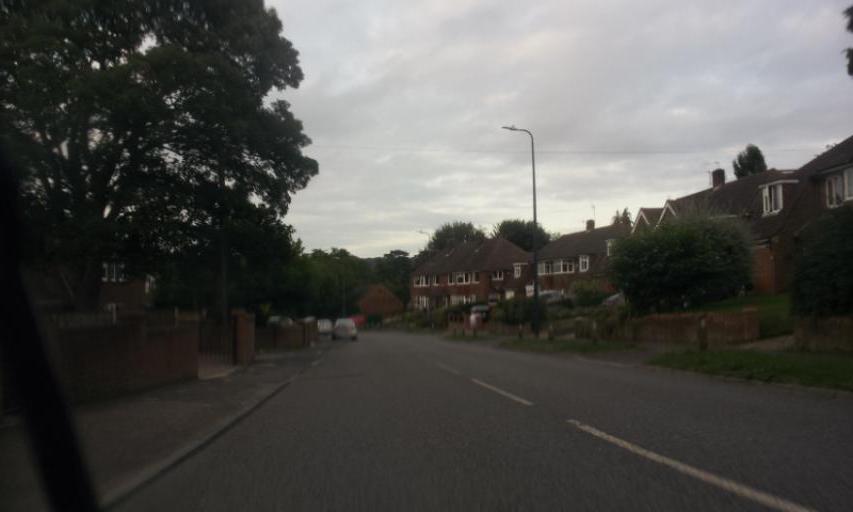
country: GB
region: England
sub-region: Kent
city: Boxley
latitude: 51.2874
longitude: 0.5348
